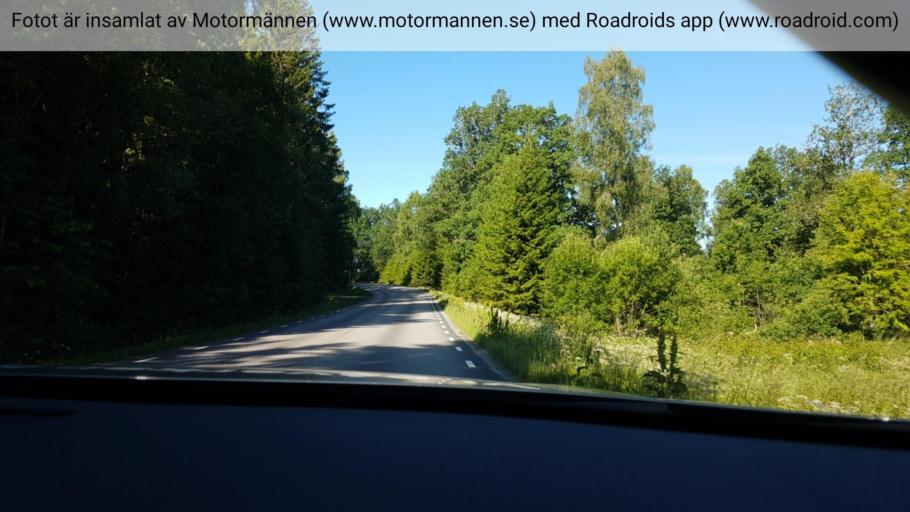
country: SE
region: Vaestra Goetaland
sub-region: Ulricehamns Kommun
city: Ulricehamn
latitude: 57.8358
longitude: 13.3232
